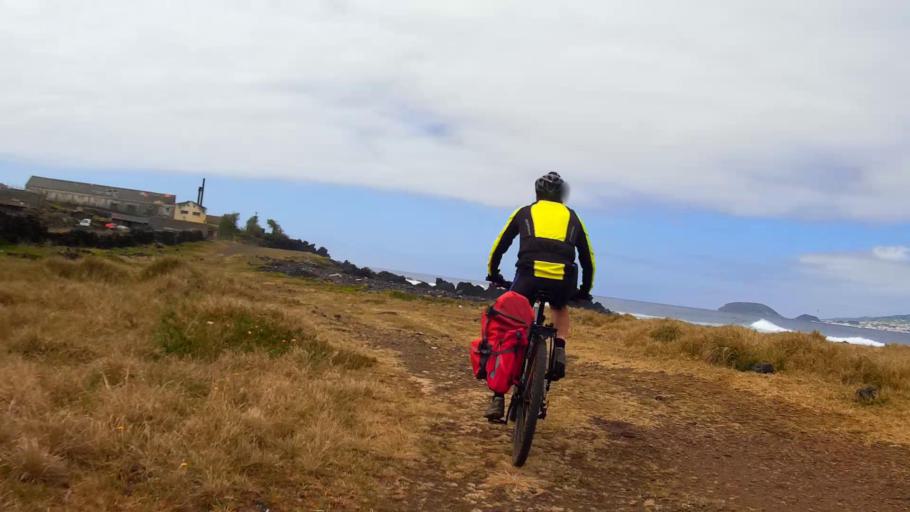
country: PT
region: Azores
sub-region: Madalena
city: Madalena
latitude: 38.5317
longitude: -28.5353
